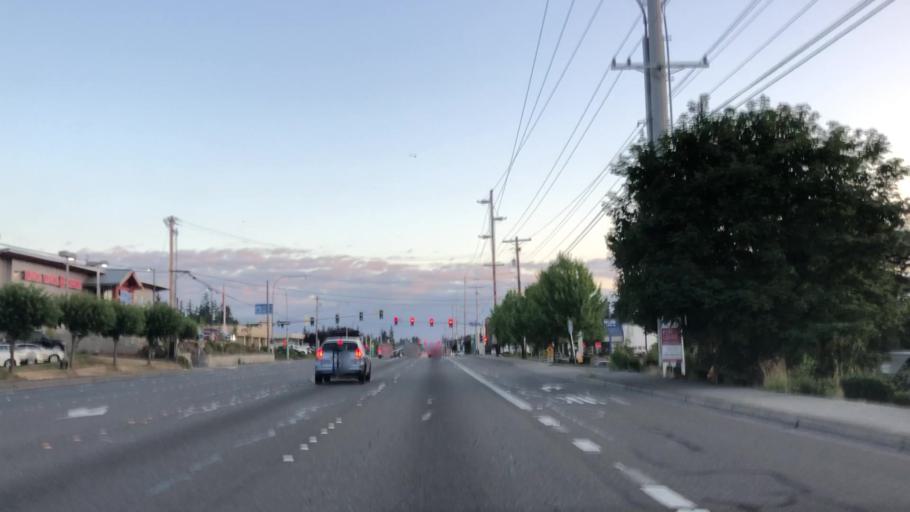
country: US
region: Washington
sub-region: Snohomish County
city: Alderwood Manor
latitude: 47.8421
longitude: -122.2971
